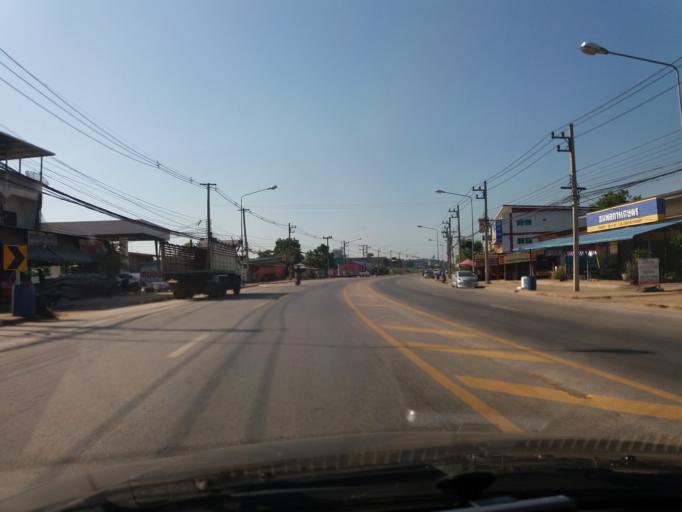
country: TH
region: Kamphaeng Phet
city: Khlong Khlung
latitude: 16.2311
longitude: 99.7333
